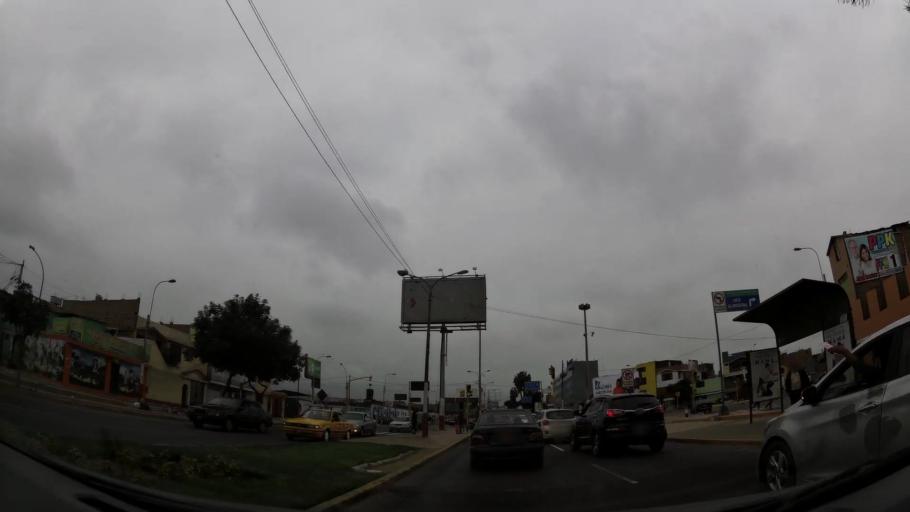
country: PE
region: Callao
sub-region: Callao
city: Callao
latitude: -12.0552
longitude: -77.1064
